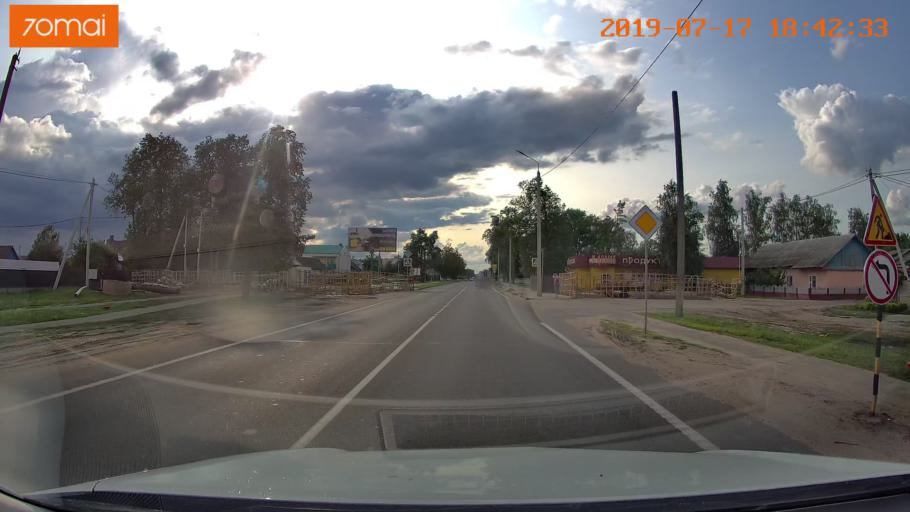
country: BY
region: Mogilev
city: Asipovichy
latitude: 53.3104
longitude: 28.6478
